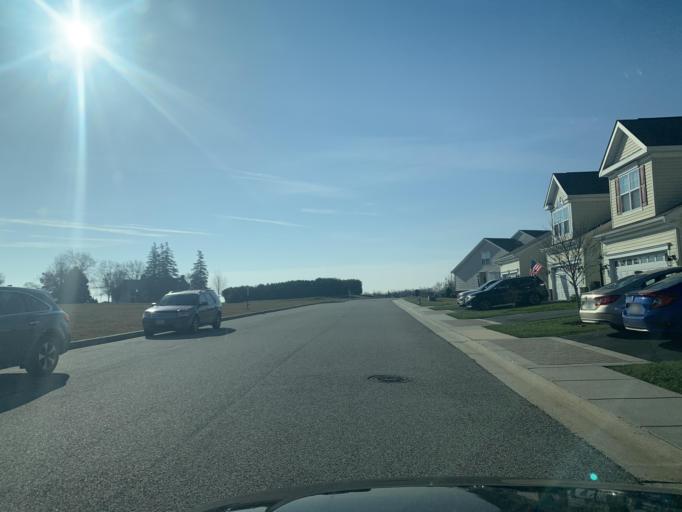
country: US
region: Maryland
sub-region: Harford County
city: Havre de Grace
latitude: 39.5520
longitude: -76.1294
